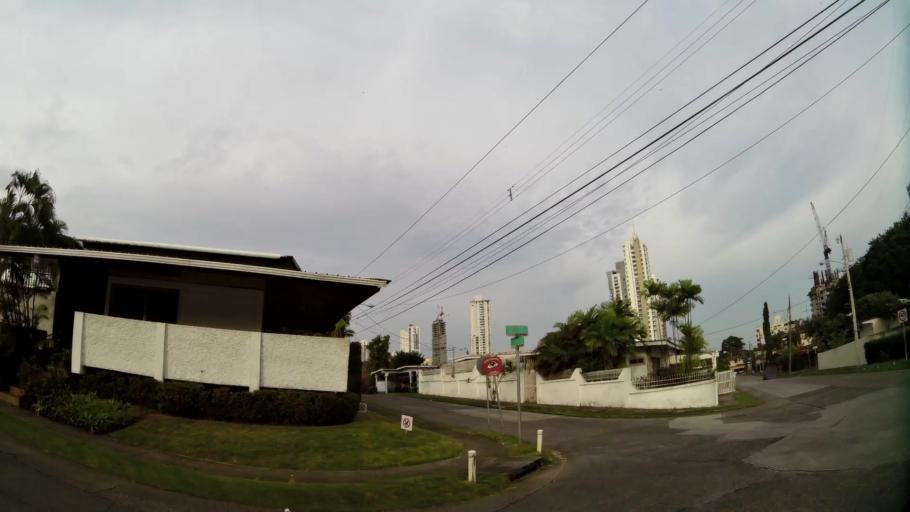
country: PA
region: Panama
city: Panama
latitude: 8.9960
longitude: -79.5011
